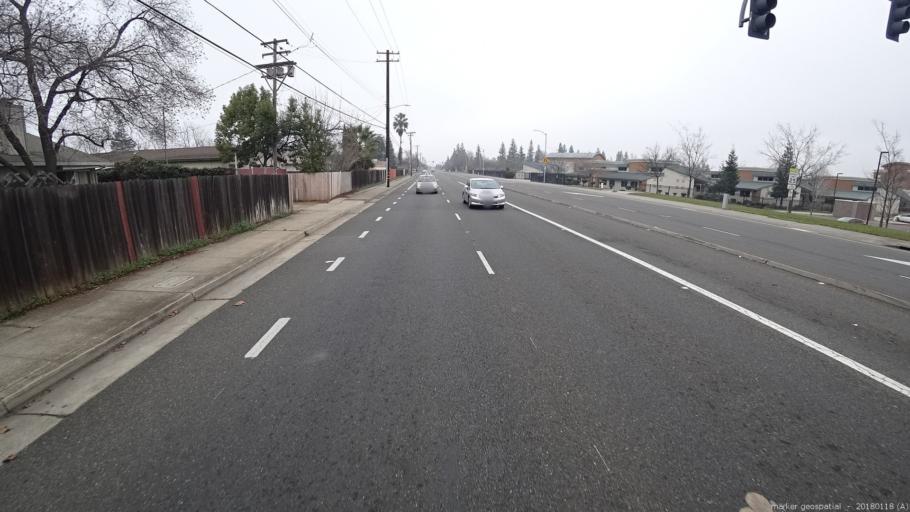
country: US
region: California
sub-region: Sacramento County
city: Rancho Cordova
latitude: 38.5641
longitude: -121.3180
